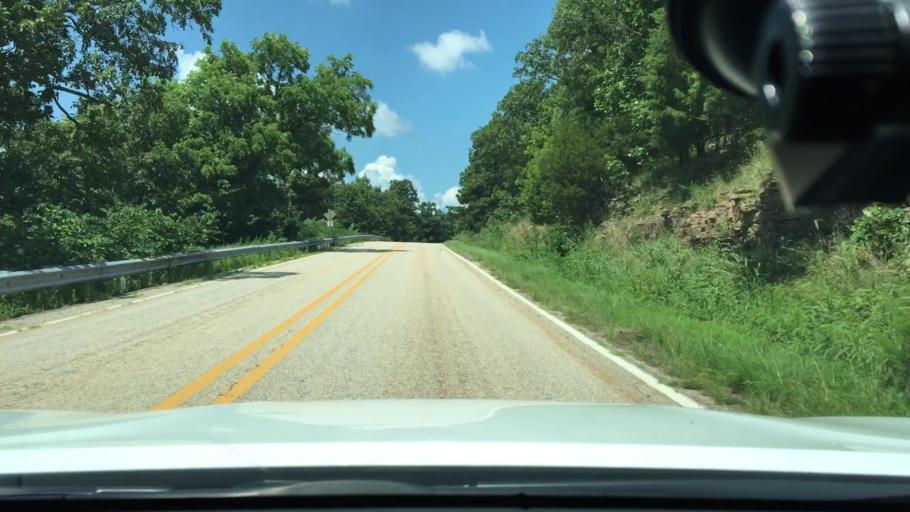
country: US
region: Arkansas
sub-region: Logan County
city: Paris
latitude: 35.1756
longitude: -93.5916
